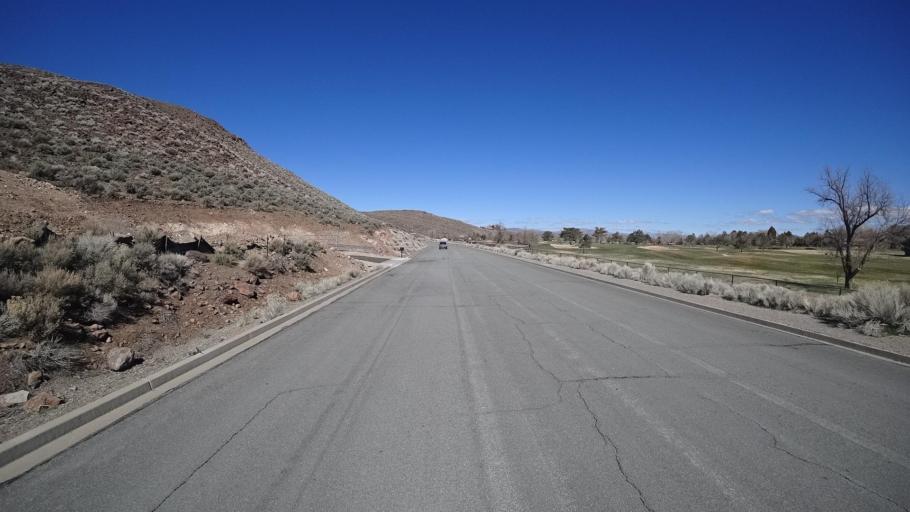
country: US
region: Nevada
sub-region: Washoe County
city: Sparks
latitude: 39.4802
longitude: -119.7279
